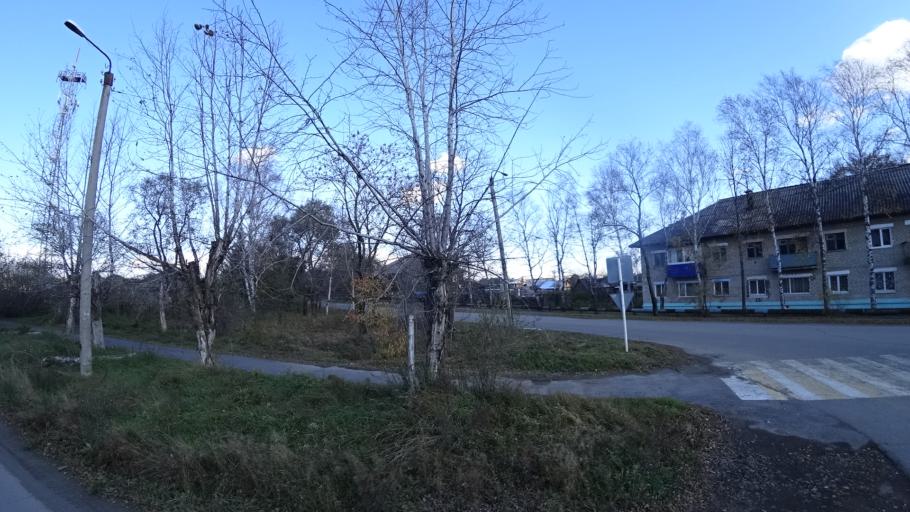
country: RU
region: Khabarovsk Krai
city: Amursk
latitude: 50.0955
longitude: 136.4982
